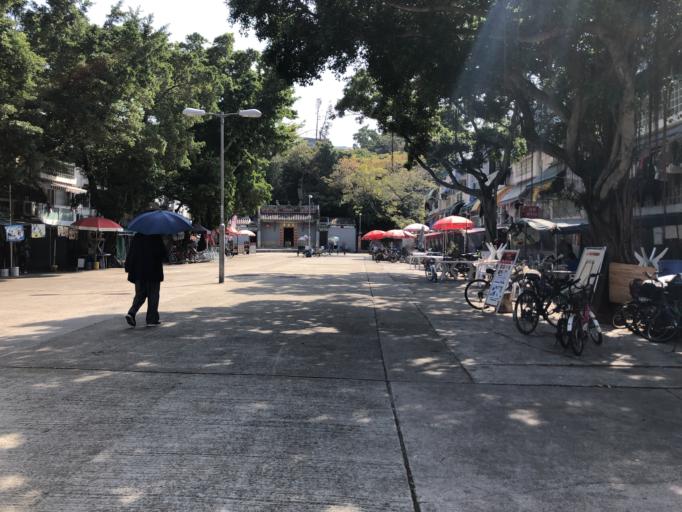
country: HK
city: Yung Shue Wan
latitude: 22.2054
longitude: 114.0270
